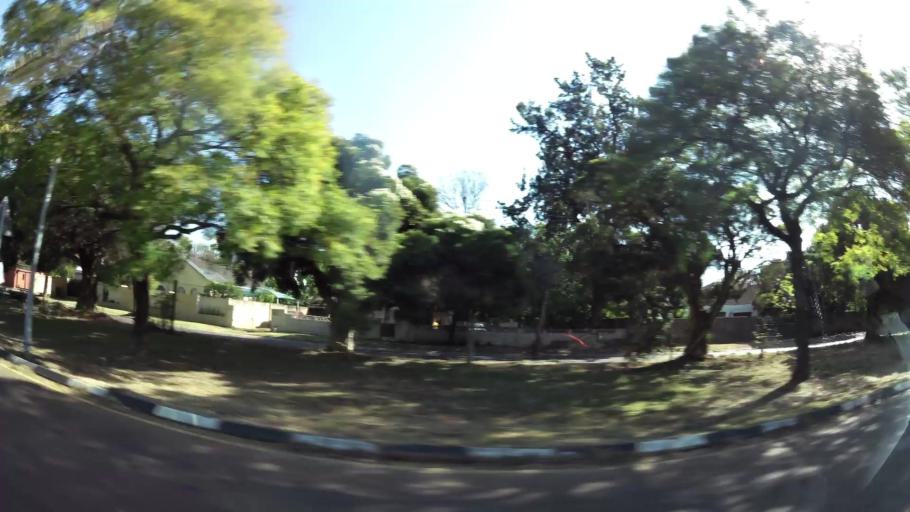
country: ZA
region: Gauteng
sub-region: City of Tshwane Metropolitan Municipality
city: Pretoria
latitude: -25.7284
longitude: 28.2584
